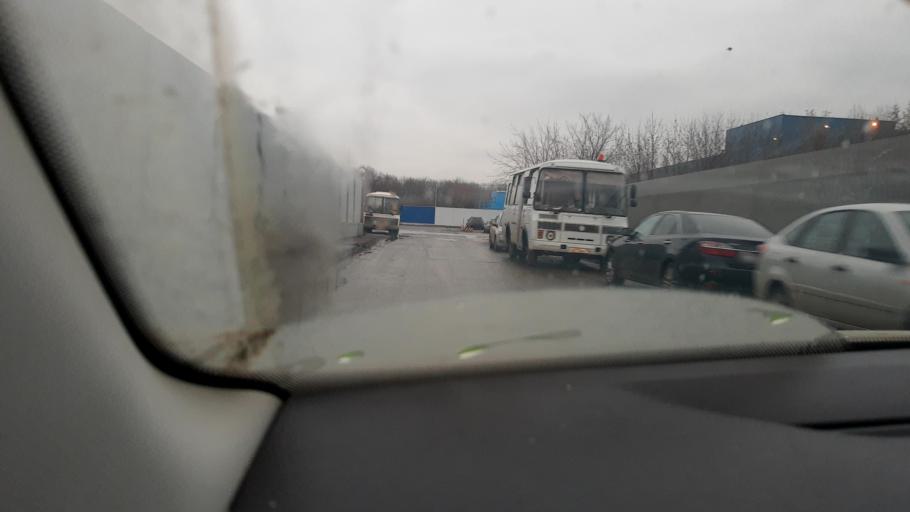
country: RU
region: Moskovskaya
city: Kur'yanovo
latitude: 55.6663
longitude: 37.7018
